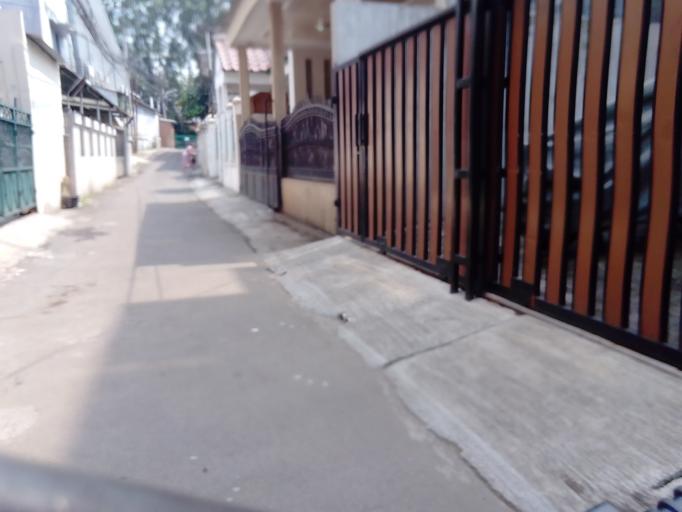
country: ID
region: Jakarta Raya
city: Jakarta
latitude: -6.2127
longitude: 106.8117
